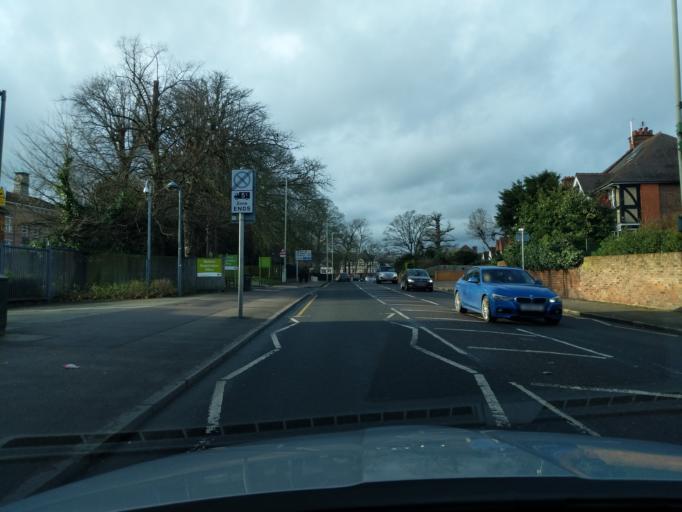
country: GB
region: England
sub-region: Hertfordshire
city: Watford
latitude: 51.6608
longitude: -0.4053
